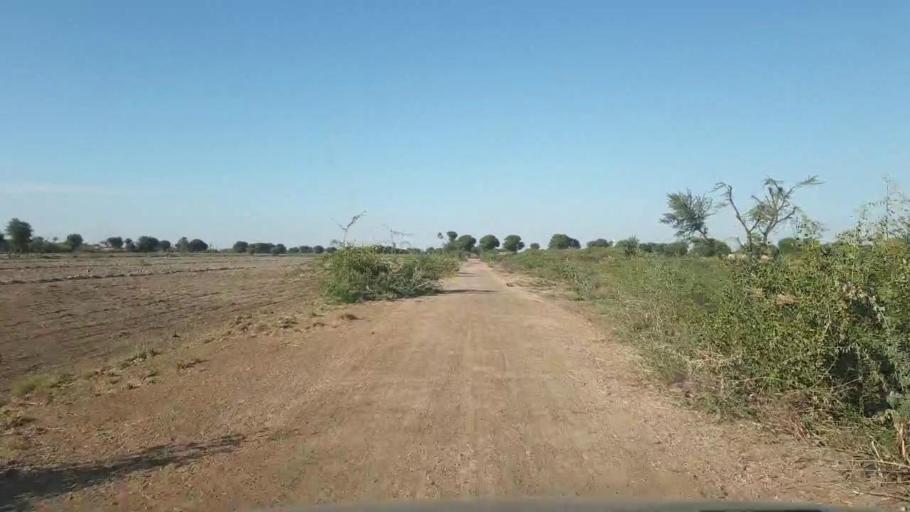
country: PK
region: Sindh
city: Dhoro Naro
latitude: 25.4315
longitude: 69.5438
